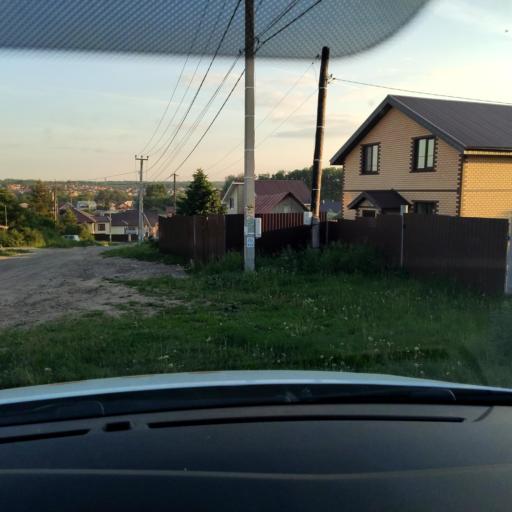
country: RU
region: Tatarstan
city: Stolbishchi
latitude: 55.7522
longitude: 49.3003
